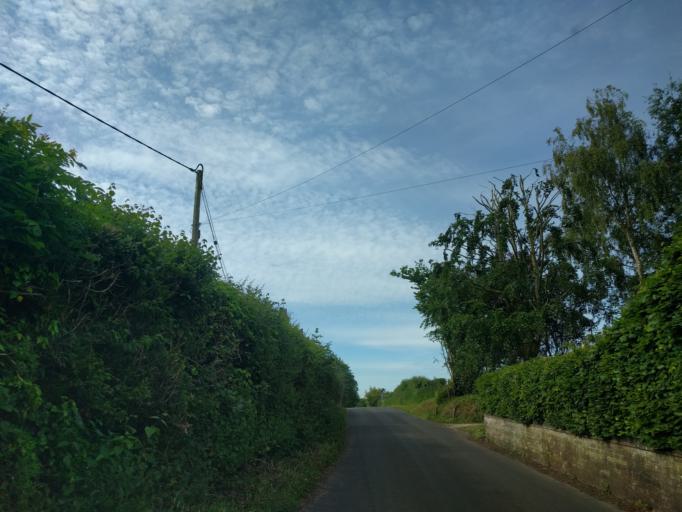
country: GB
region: England
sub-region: Wiltshire
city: Melksham
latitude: 51.3291
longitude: -2.1357
